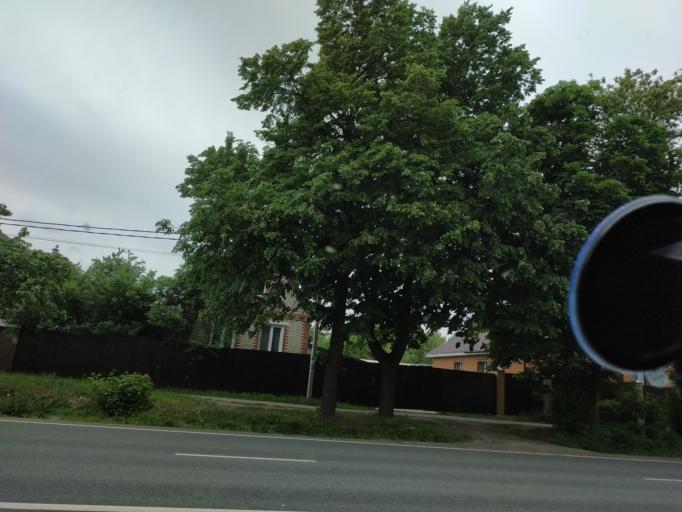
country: RU
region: Moskovskaya
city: Ostrovtsy
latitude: 55.5569
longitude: 38.0555
